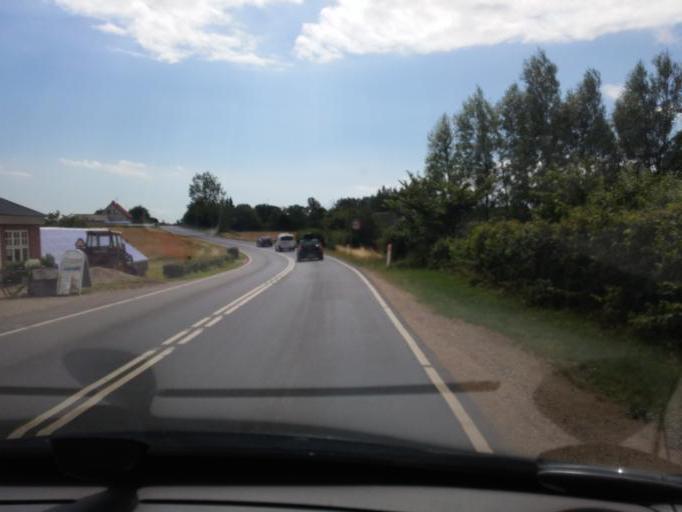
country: DK
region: South Denmark
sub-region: Langeland Kommune
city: Rudkobing
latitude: 54.8918
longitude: 10.7346
